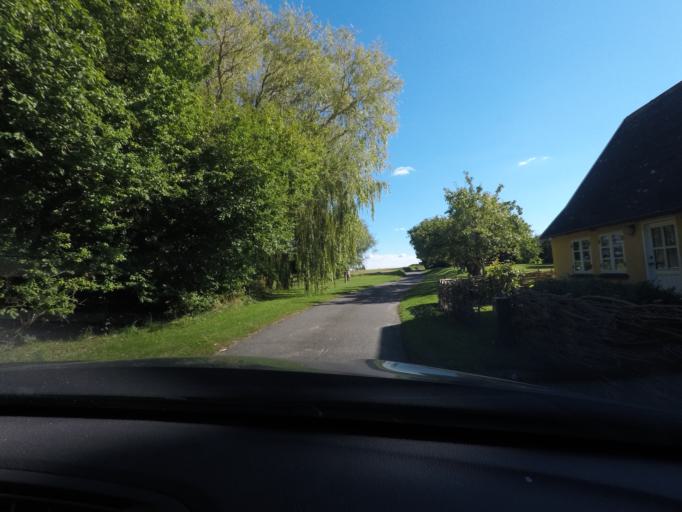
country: DK
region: Zealand
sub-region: Guldborgsund Kommune
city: Sakskobing
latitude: 54.9683
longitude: 11.5363
